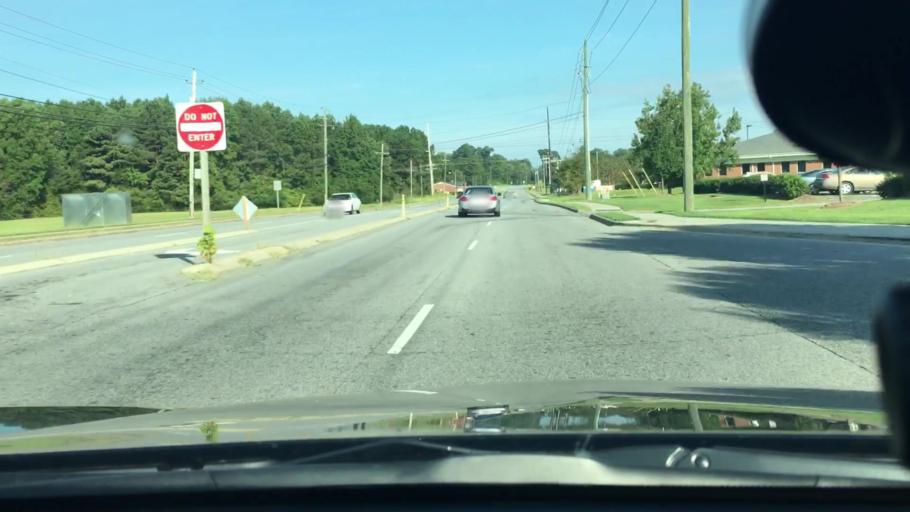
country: US
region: North Carolina
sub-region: Pitt County
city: Greenville
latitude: 35.6175
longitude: -77.4114
